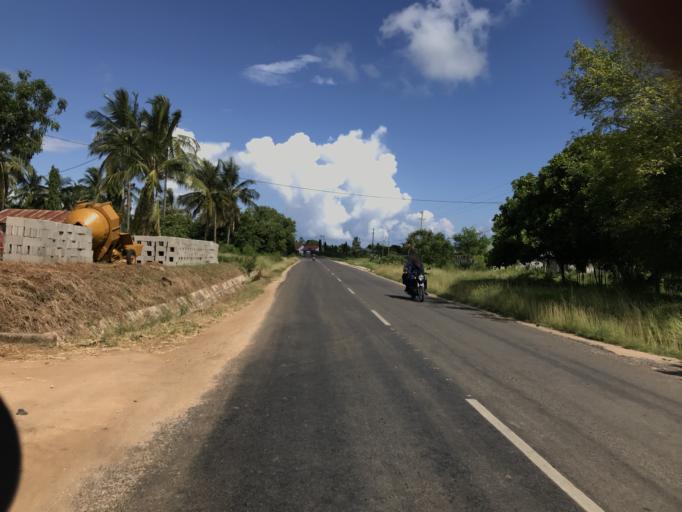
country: TZ
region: Dar es Salaam
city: Dar es Salaam
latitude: -6.8814
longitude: 39.4165
